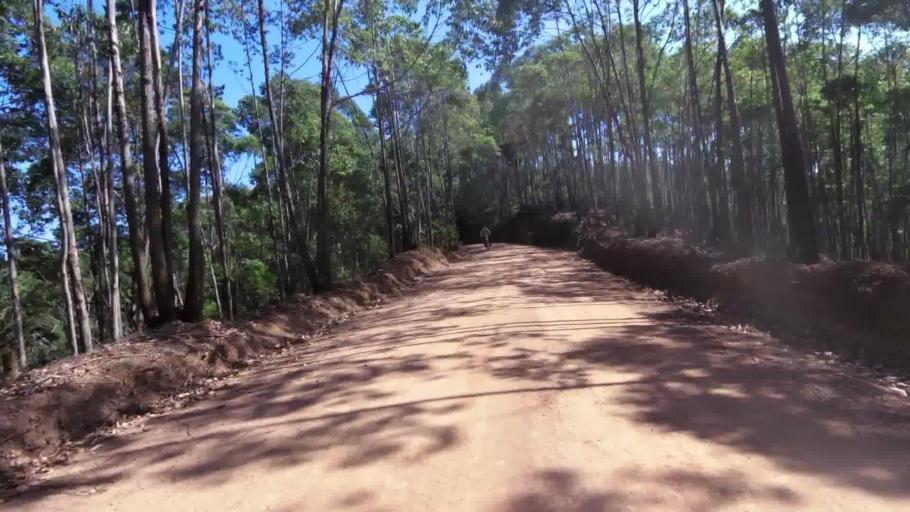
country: BR
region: Espirito Santo
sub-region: Alfredo Chaves
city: Alfredo Chaves
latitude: -20.5173
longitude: -40.8771
